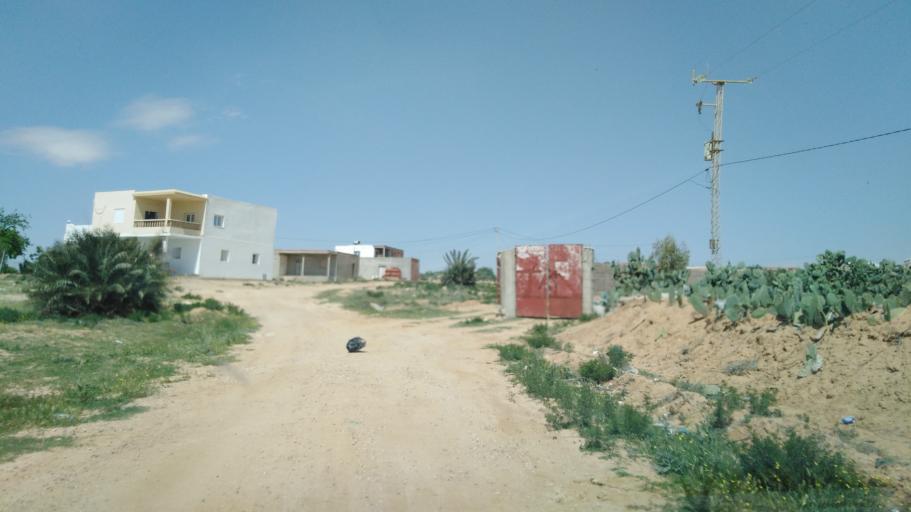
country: TN
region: Safaqis
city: Sfax
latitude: 34.7629
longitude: 10.5222
